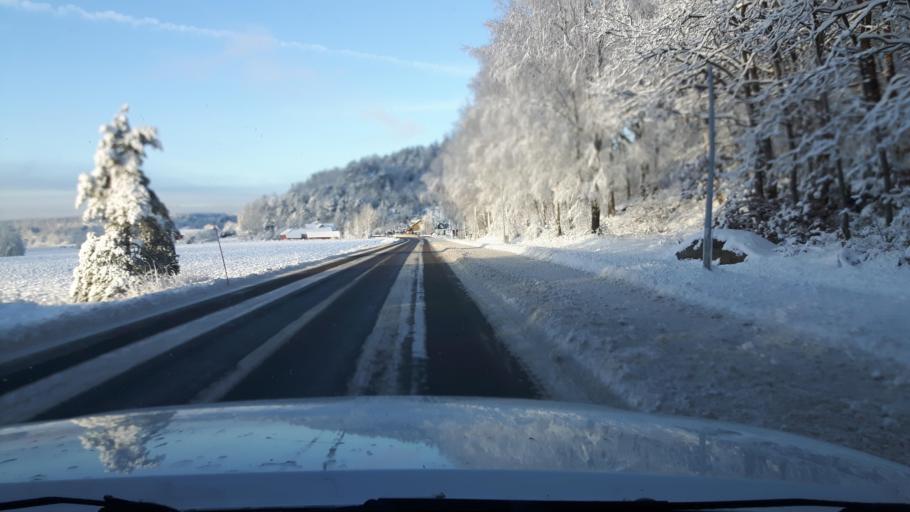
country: SE
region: Vaestra Goetaland
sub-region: Molndal
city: Lindome
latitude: 57.5421
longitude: 12.1424
